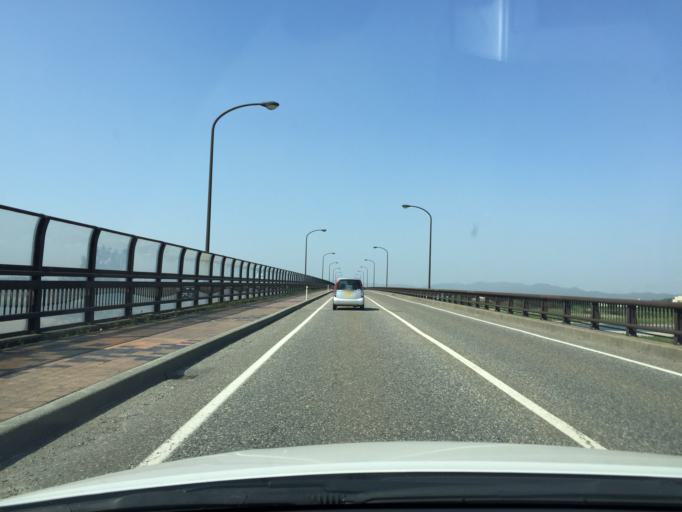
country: JP
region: Niigata
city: Gosen
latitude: 37.7532
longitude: 139.2263
